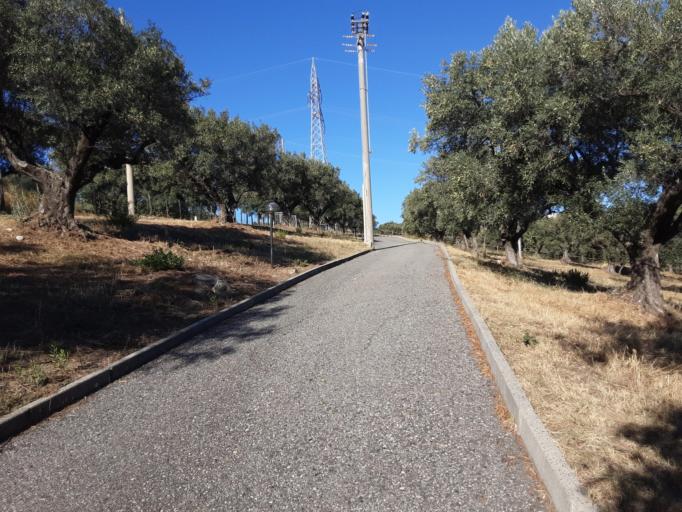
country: IT
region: Calabria
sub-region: Provincia di Catanzaro
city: Staletti
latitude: 38.7647
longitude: 16.5539
